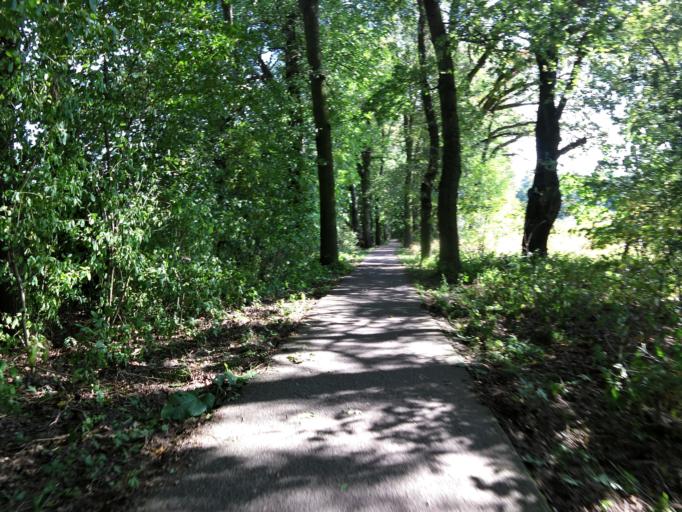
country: DE
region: Saxony-Anhalt
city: Dessau
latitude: 51.8571
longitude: 12.2463
